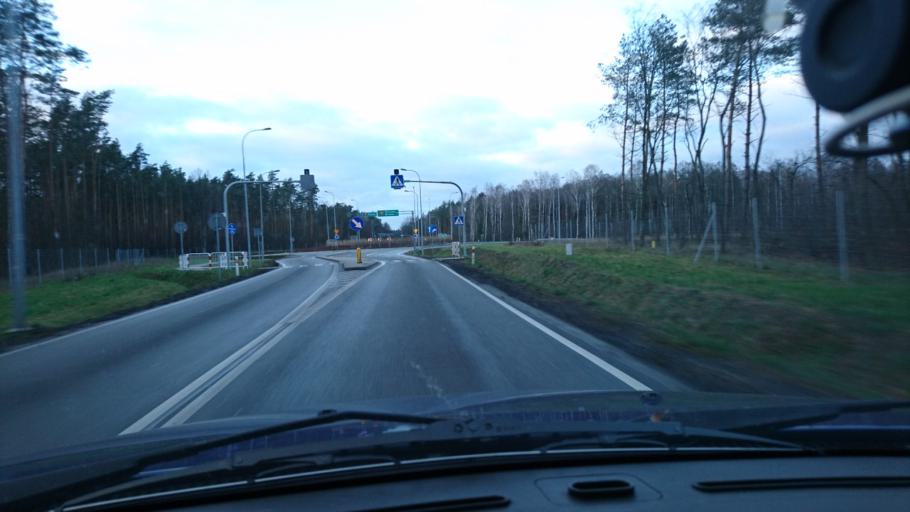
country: PL
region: Greater Poland Voivodeship
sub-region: Powiat kepinski
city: Kepno
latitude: 51.3301
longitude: 17.9596
